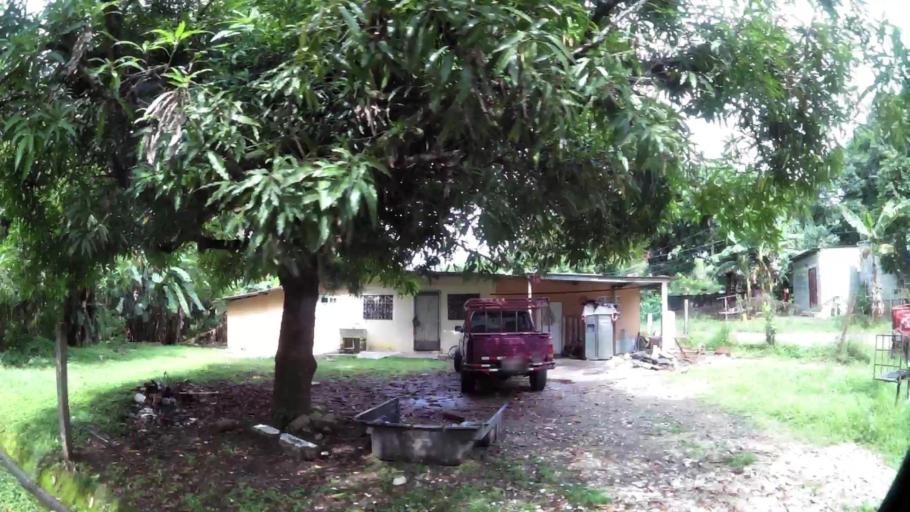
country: PA
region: Panama
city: Tocumen
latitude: 9.0962
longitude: -79.3664
